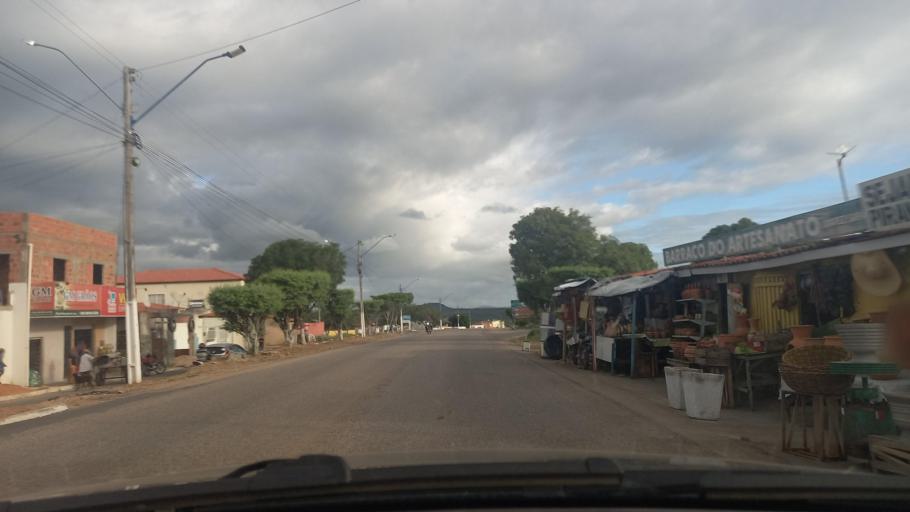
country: BR
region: Sergipe
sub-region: Caninde De Sao Francisco
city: Caninde de Sao Francisco
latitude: -9.6104
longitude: -37.7618
